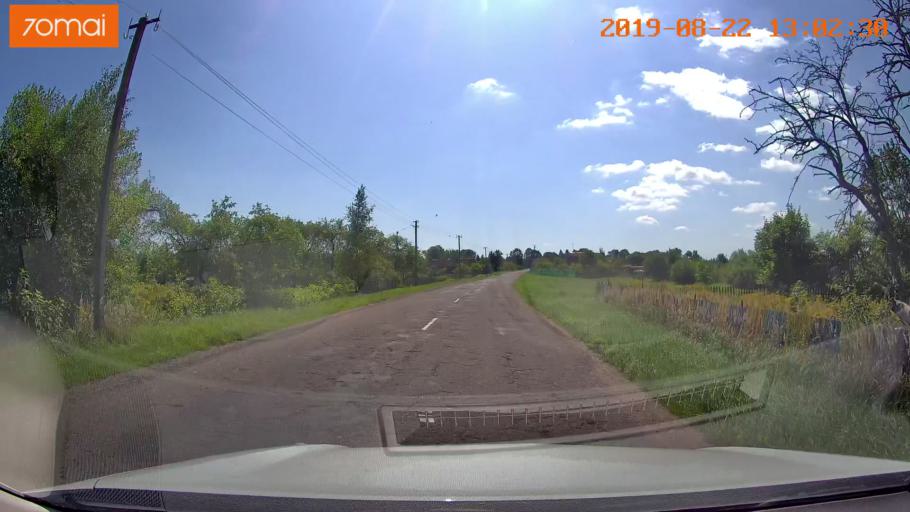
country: BY
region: Minsk
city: Prawdzinski
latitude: 53.3885
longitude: 27.8253
